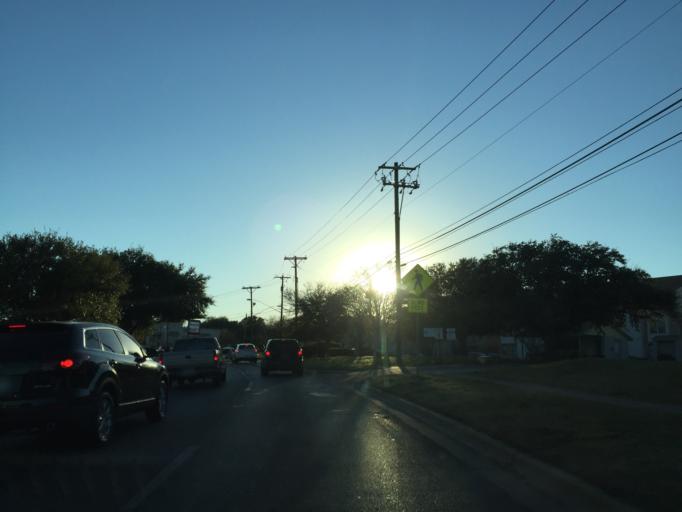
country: US
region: Texas
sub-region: Travis County
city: Austin
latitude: 30.3301
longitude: -97.6894
